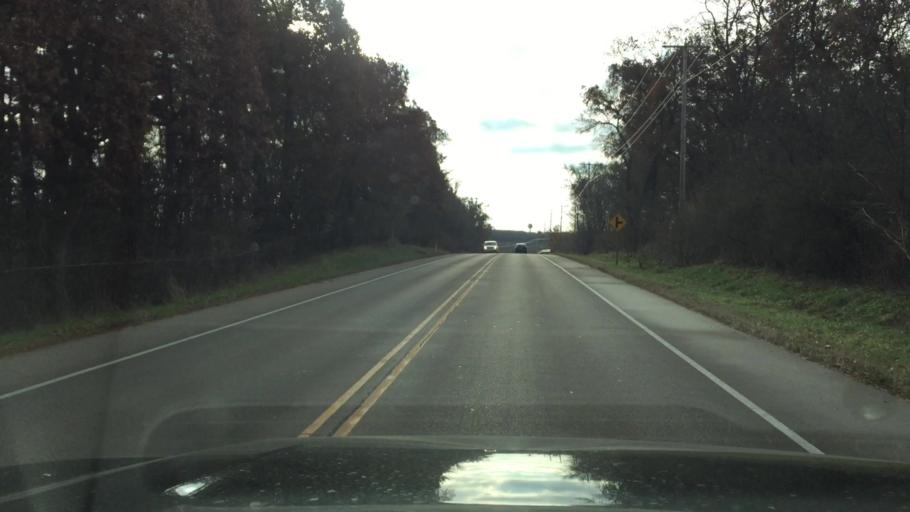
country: US
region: Wisconsin
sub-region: Walworth County
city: Williams Bay
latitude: 42.5900
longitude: -88.5323
